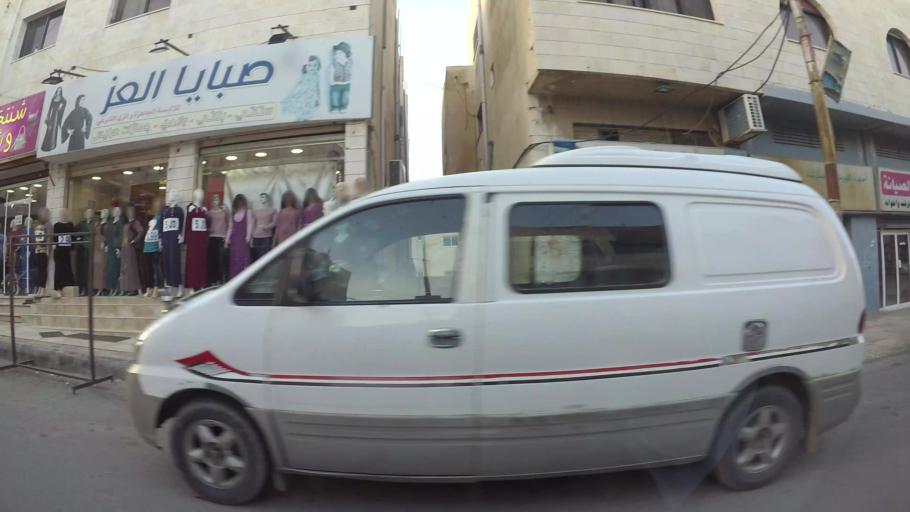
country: JO
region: Amman
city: Al Bunayyat ash Shamaliyah
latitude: 31.9059
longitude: 35.9105
